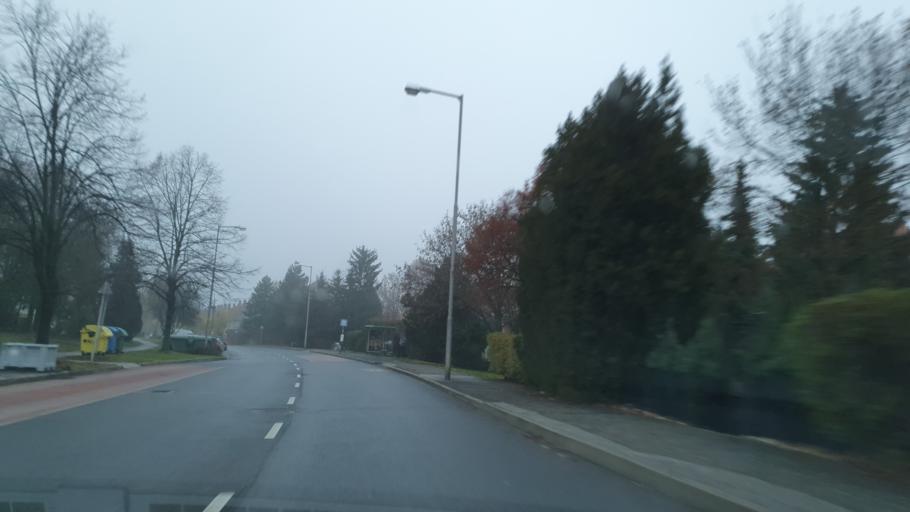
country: HU
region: Veszprem
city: Veszprem
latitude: 47.0919
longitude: 17.9290
